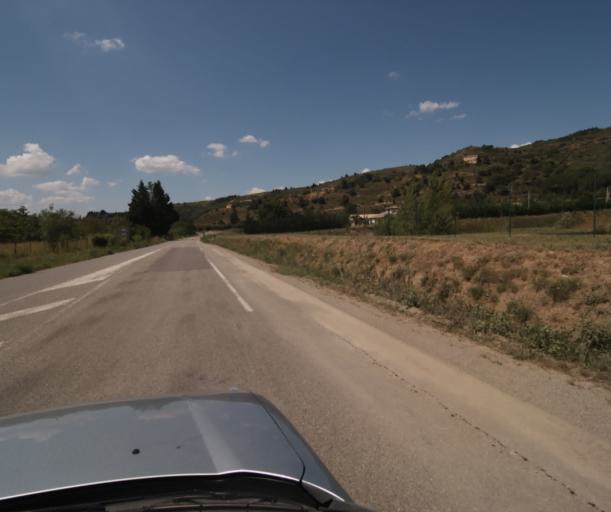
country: FR
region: Languedoc-Roussillon
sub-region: Departement de l'Aude
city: Limoux
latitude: 43.0436
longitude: 2.2449
